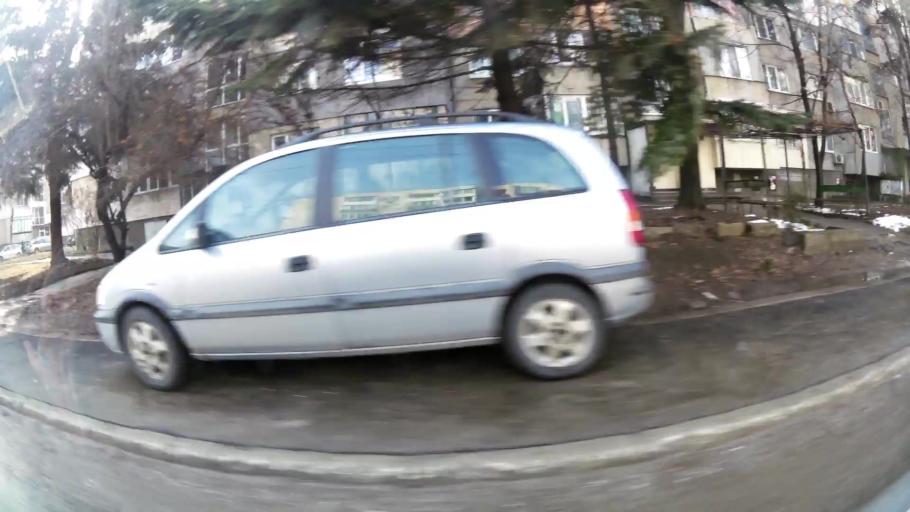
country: BG
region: Sofia-Capital
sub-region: Stolichna Obshtina
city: Sofia
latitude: 42.7204
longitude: 23.2659
